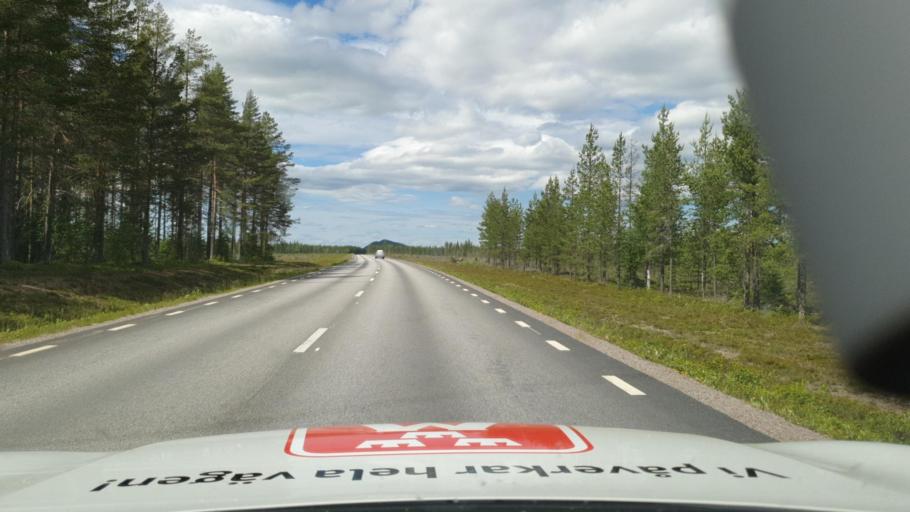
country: SE
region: Vaesterbotten
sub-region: Skelleftea Kommun
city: Langsele
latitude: 65.1227
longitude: 19.9442
